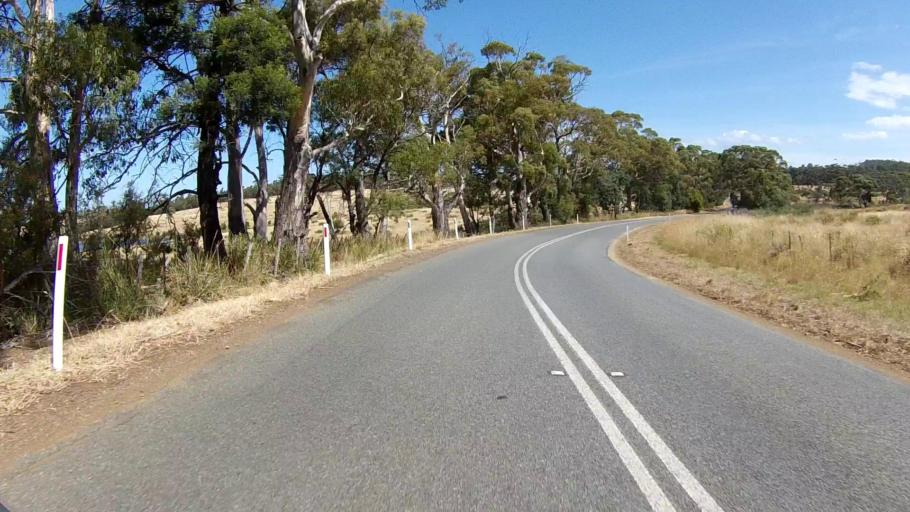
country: AU
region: Tasmania
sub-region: Sorell
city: Sorell
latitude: -42.3036
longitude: 147.9701
